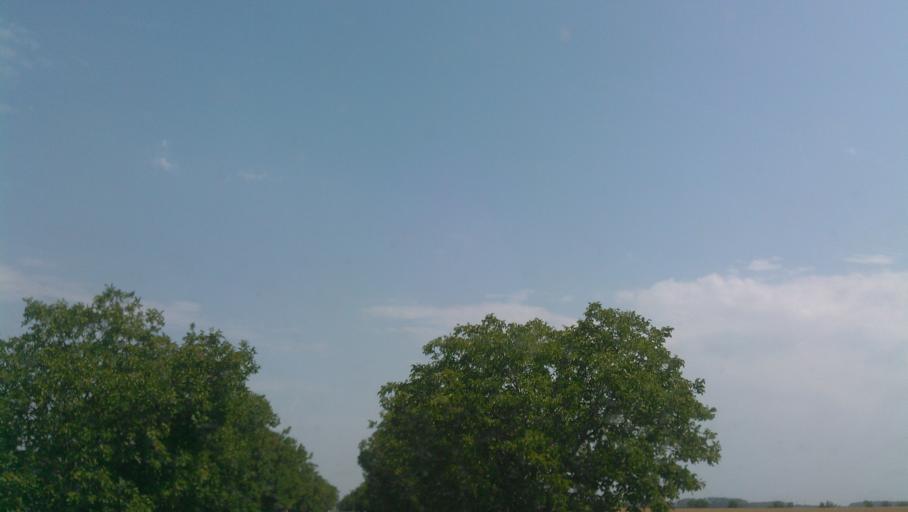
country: SK
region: Trnavsky
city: Dunajska Streda
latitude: 48.0334
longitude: 17.5370
